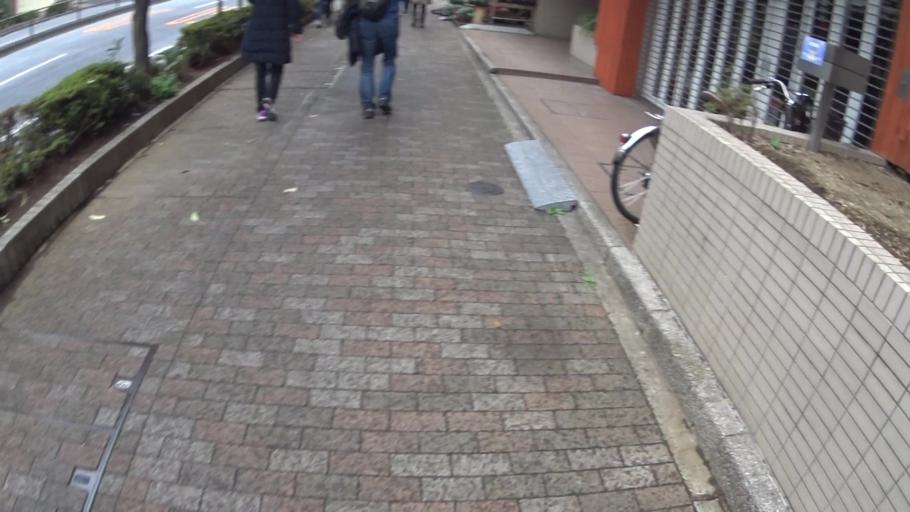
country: JP
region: Tokyo
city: Tokyo
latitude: 35.6976
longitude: 139.7135
